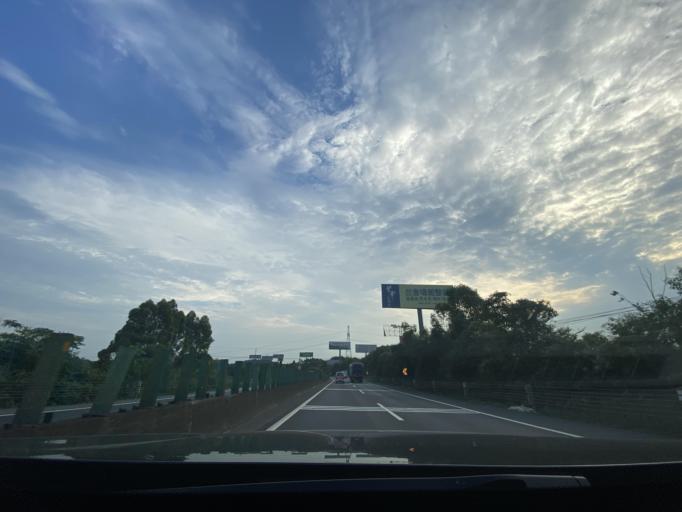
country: CN
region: Sichuan
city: Luojiang
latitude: 31.4032
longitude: 104.5690
